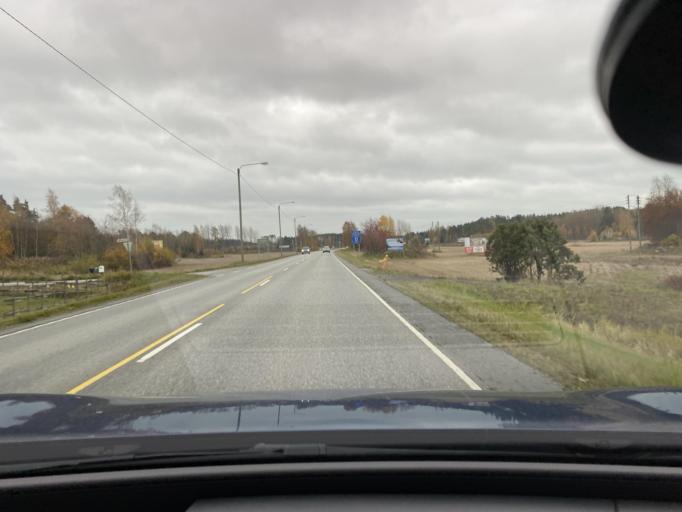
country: FI
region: Varsinais-Suomi
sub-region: Vakka-Suomi
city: Pyhaeranta
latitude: 60.9829
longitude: 21.5891
